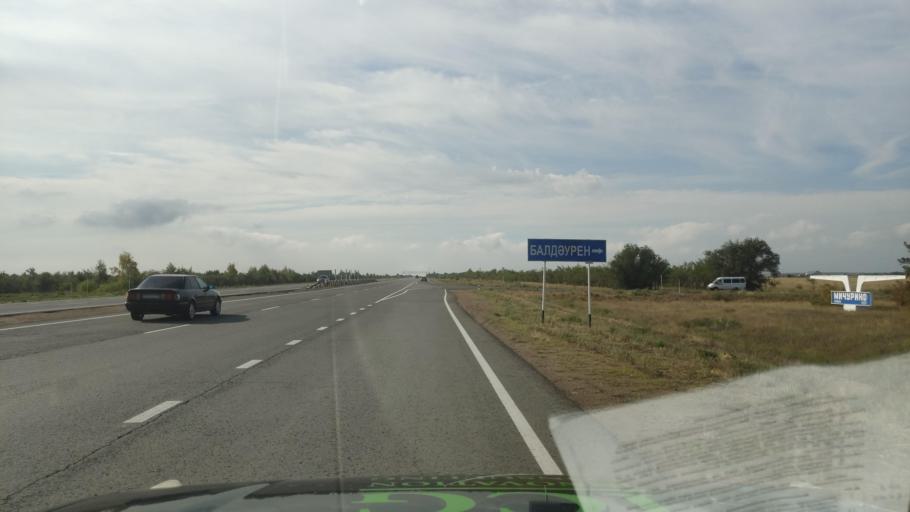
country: KZ
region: Pavlodar
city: Leninskiy
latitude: 52.4789
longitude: 76.8369
